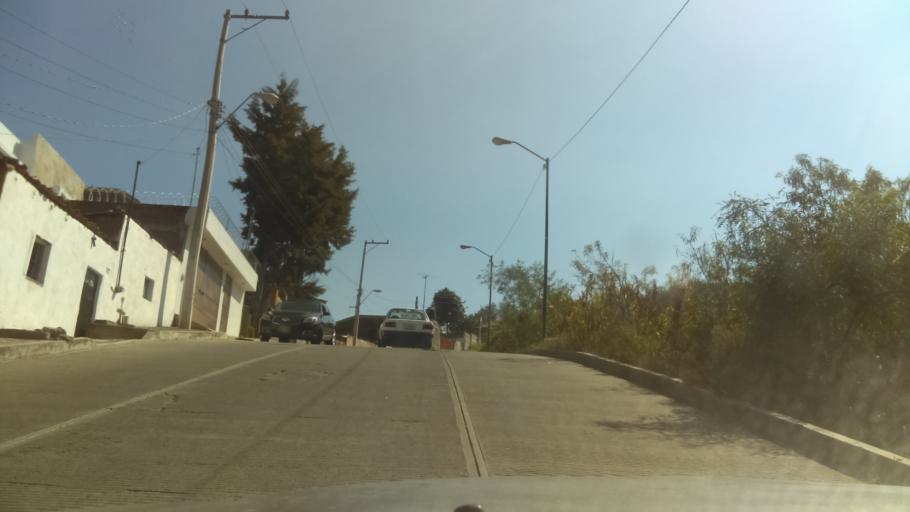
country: MX
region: Michoacan
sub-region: Morelia
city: Montana Monarca (Punta Altozano)
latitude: 19.6680
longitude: -101.1884
